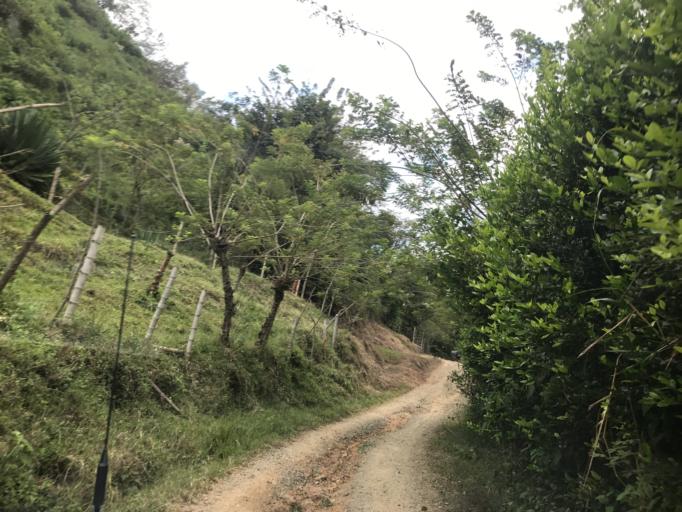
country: CO
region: Valle del Cauca
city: Obando
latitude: 4.5494
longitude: -75.9164
